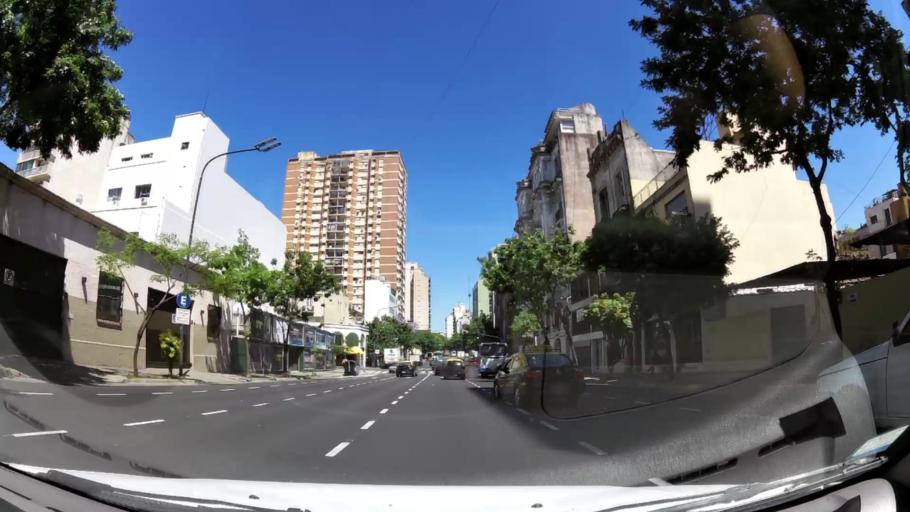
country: AR
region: Buenos Aires F.D.
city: Buenos Aires
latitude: -34.6172
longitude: -58.3711
